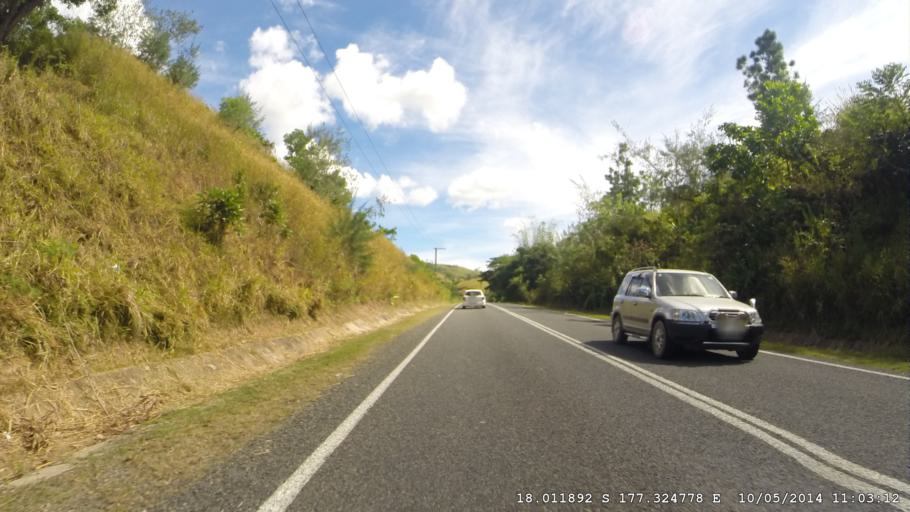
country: FJ
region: Western
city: Nadi
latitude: -18.0119
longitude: 177.3248
